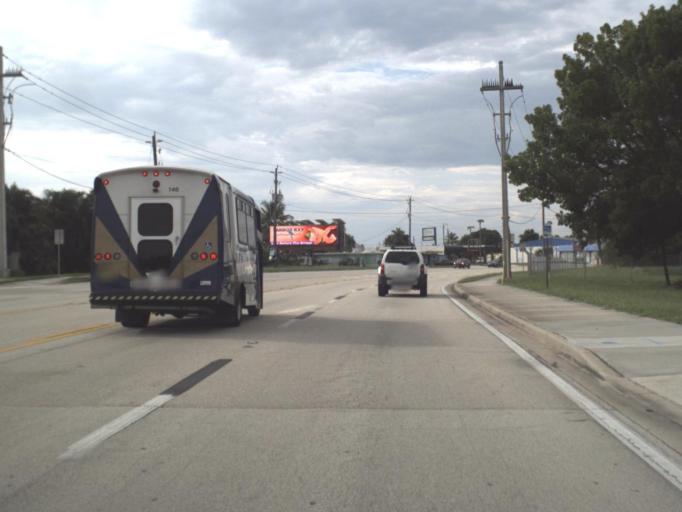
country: US
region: Florida
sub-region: Lee County
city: Harlem Heights
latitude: 26.4867
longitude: -81.9432
